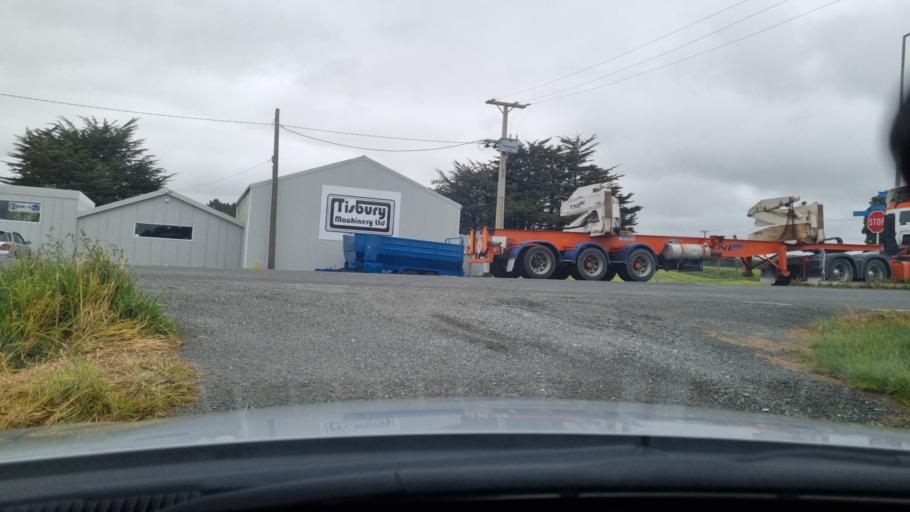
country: NZ
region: Southland
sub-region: Invercargill City
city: Invercargill
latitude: -46.4441
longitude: 168.3990
